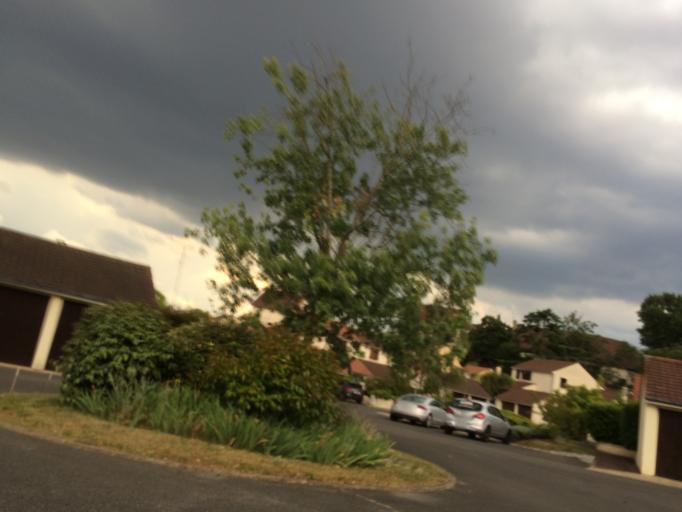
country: FR
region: Ile-de-France
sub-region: Departement de l'Essonne
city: Verrieres-le-Buisson
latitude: 48.7539
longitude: 2.2645
